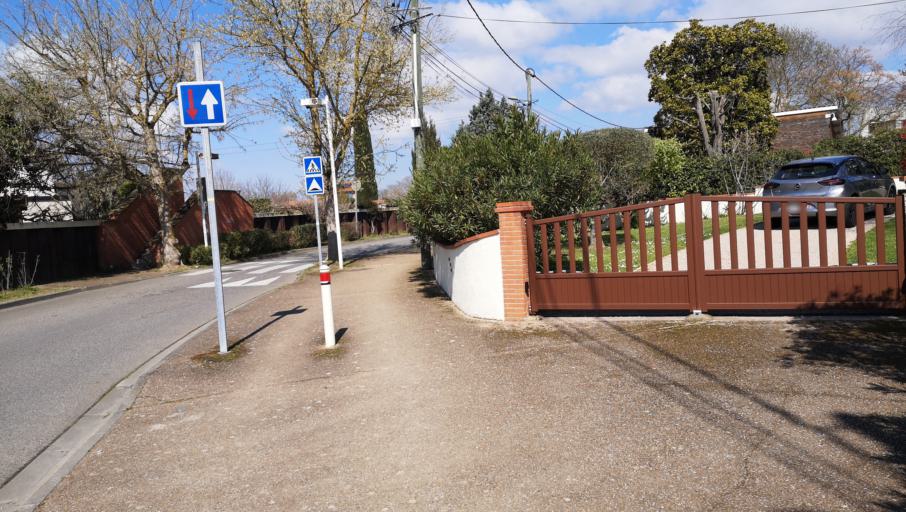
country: FR
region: Midi-Pyrenees
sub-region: Departement de la Haute-Garonne
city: Blagnac
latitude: 43.6422
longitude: 1.3995
